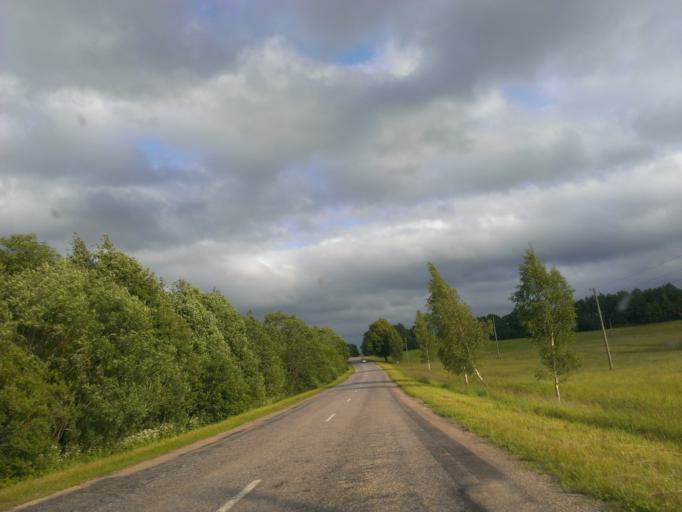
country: LV
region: Aizpute
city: Aizpute
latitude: 56.7116
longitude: 21.7644
